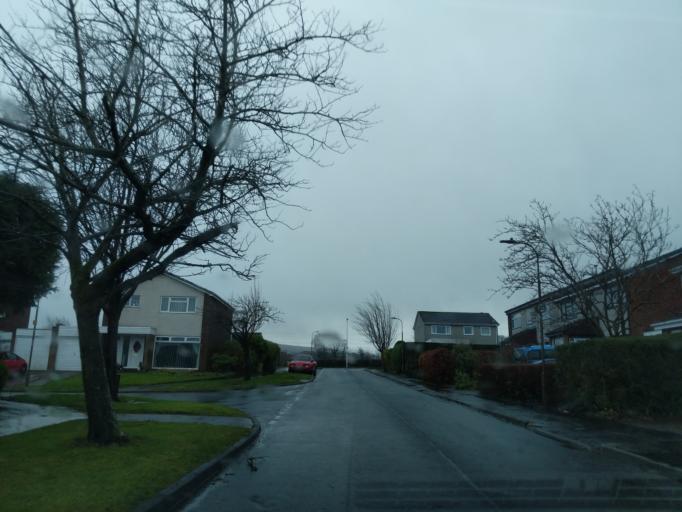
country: GB
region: Scotland
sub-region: Edinburgh
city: Balerno
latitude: 55.8764
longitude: -3.3411
